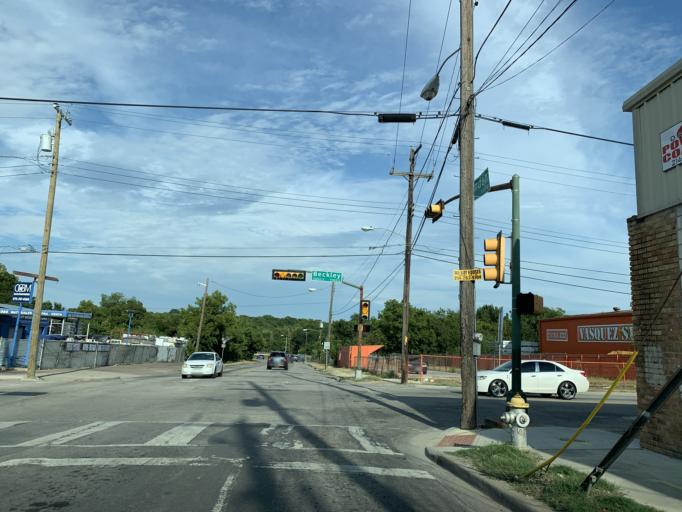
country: US
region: Texas
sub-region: Dallas County
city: Dallas
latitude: 32.7345
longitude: -96.8230
